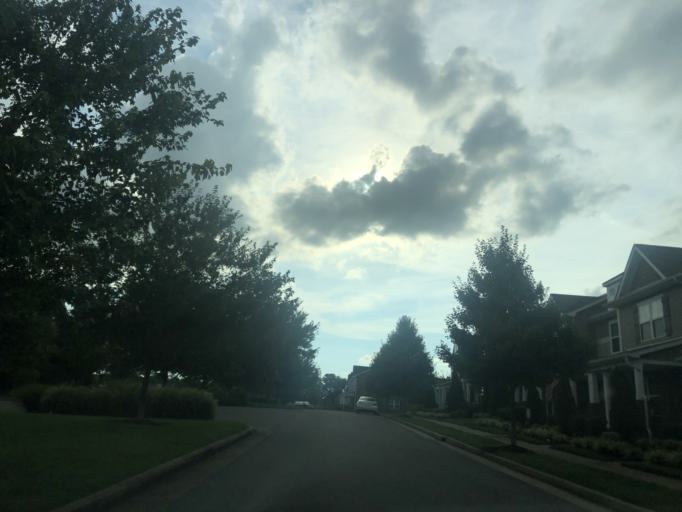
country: US
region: Tennessee
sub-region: Davidson County
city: Lakewood
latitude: 36.1694
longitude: -86.6197
